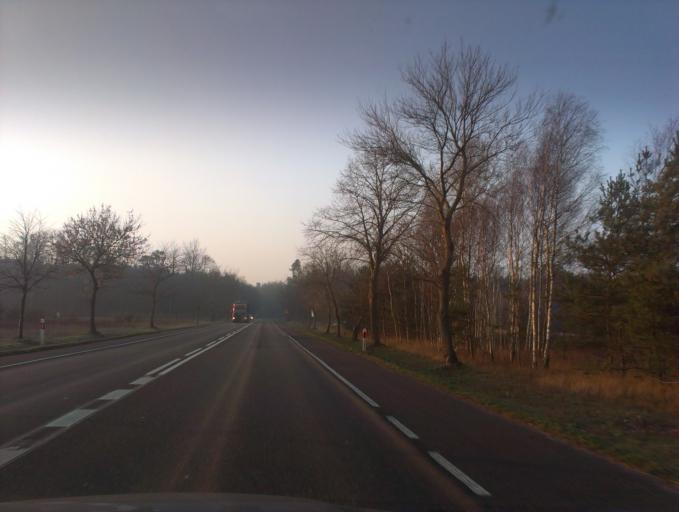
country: PL
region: Greater Poland Voivodeship
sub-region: Powiat obornicki
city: Rogozno
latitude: 52.7274
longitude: 16.9372
